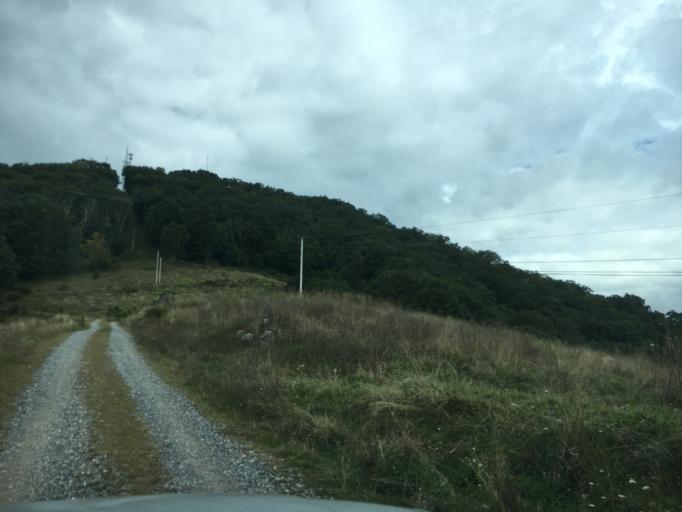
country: US
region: North Carolina
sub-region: Haywood County
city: Clyde
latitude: 35.5649
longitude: -82.9104
